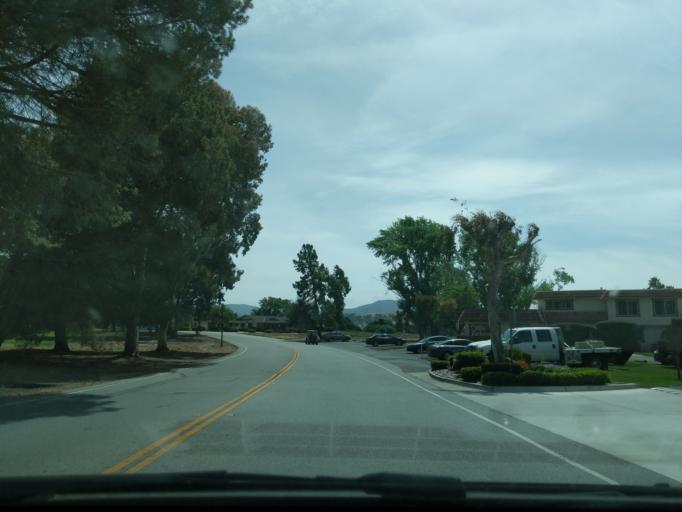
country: US
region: California
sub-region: San Benito County
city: Ridgemark
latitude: 36.8129
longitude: -121.3654
